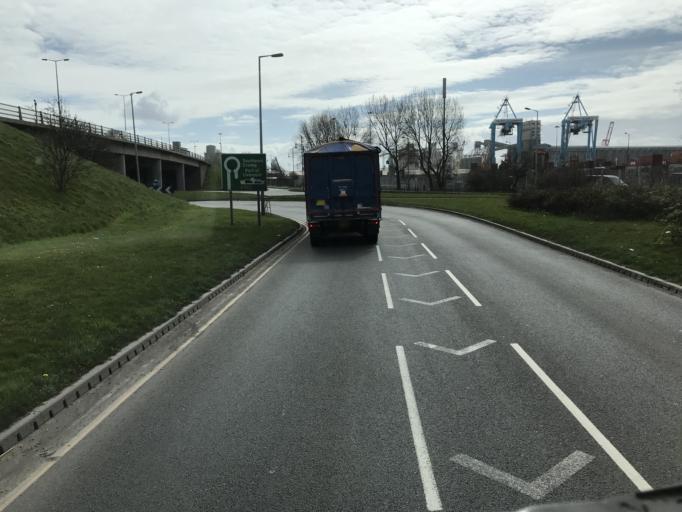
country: GB
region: England
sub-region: Sefton
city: Bootle
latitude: 53.4653
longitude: -3.0176
